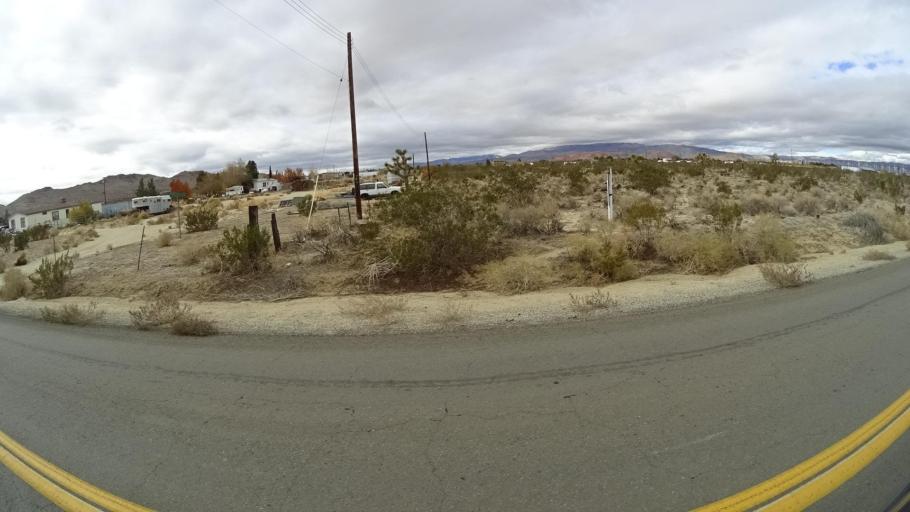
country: US
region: California
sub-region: Kern County
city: Rosamond
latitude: 34.9417
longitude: -118.2125
